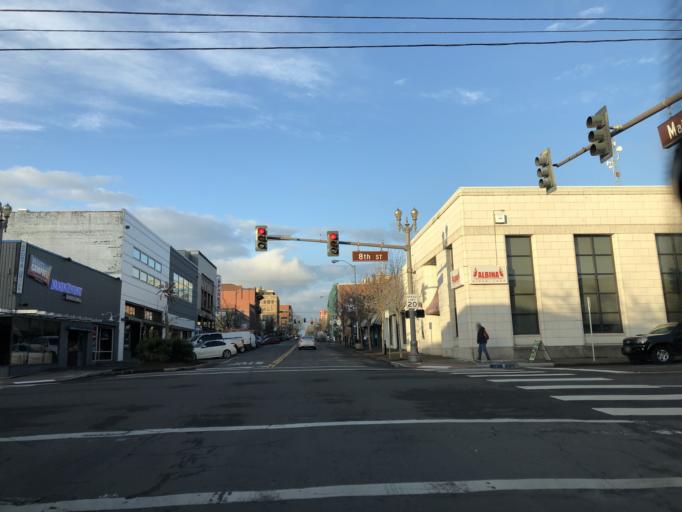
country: US
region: Washington
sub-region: Clark County
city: Vancouver
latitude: 45.6271
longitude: -122.6716
